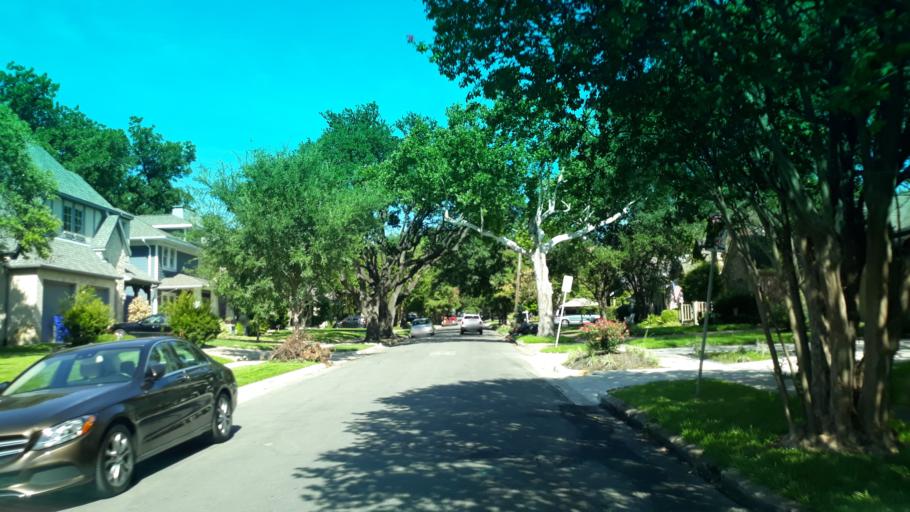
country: US
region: Texas
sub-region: Dallas County
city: Highland Park
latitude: 32.8172
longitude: -96.7610
